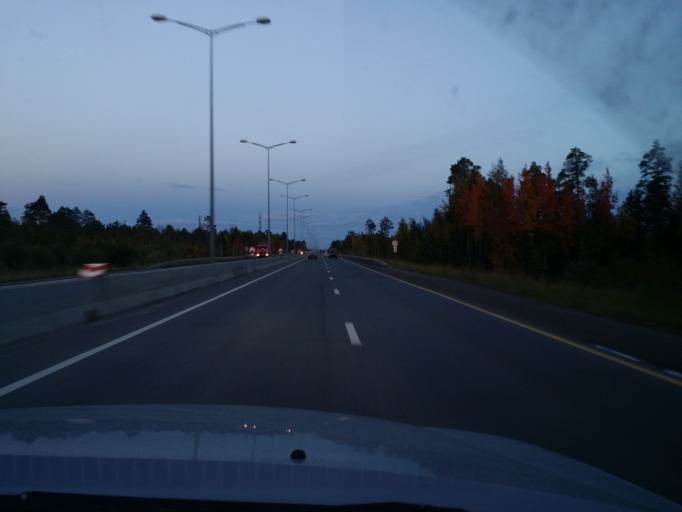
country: RU
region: Khanty-Mansiyskiy Avtonomnyy Okrug
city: Nizhnevartovsk
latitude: 61.0029
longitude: 76.4153
